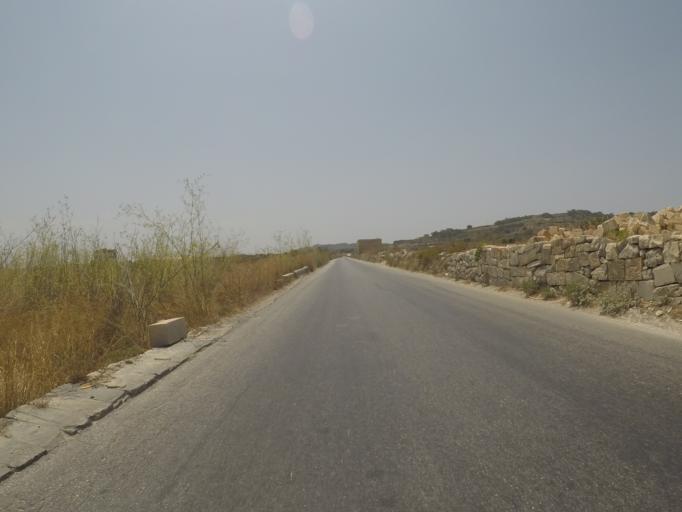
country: MT
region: Ir-Rabat
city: Rabat
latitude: 35.8735
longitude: 14.4139
